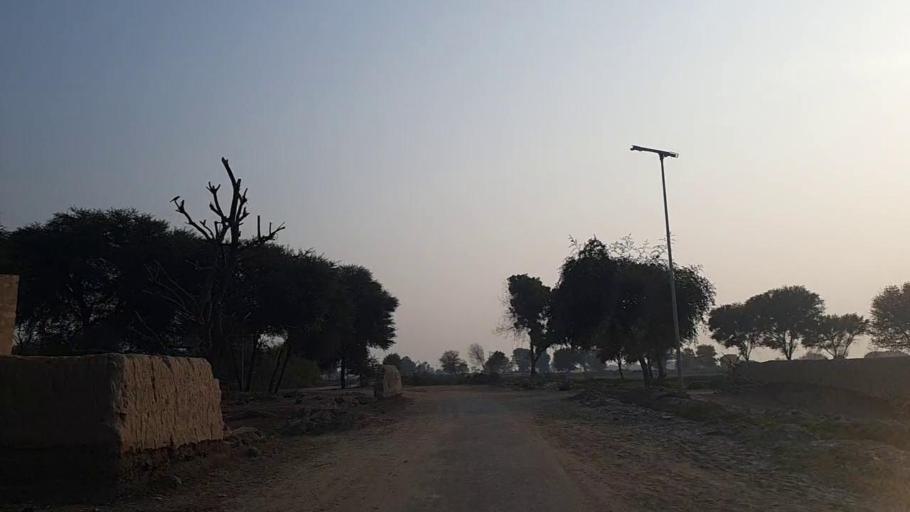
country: PK
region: Sindh
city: Nawabshah
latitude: 26.2096
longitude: 68.4711
